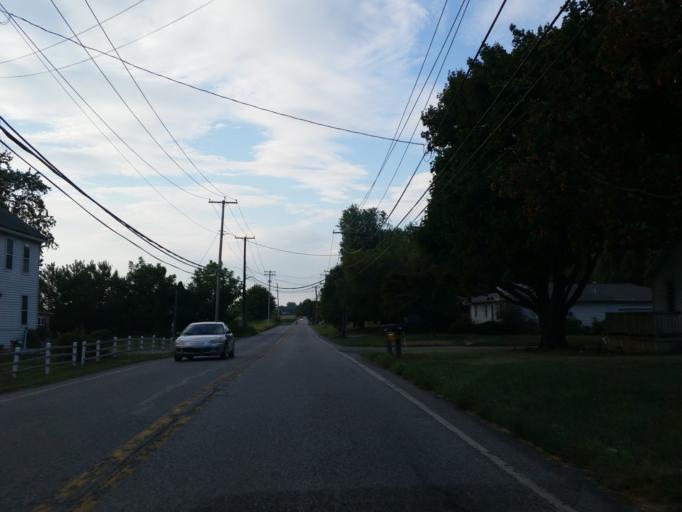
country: US
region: Pennsylvania
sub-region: Lebanon County
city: Campbelltown
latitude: 40.2890
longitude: -76.5746
